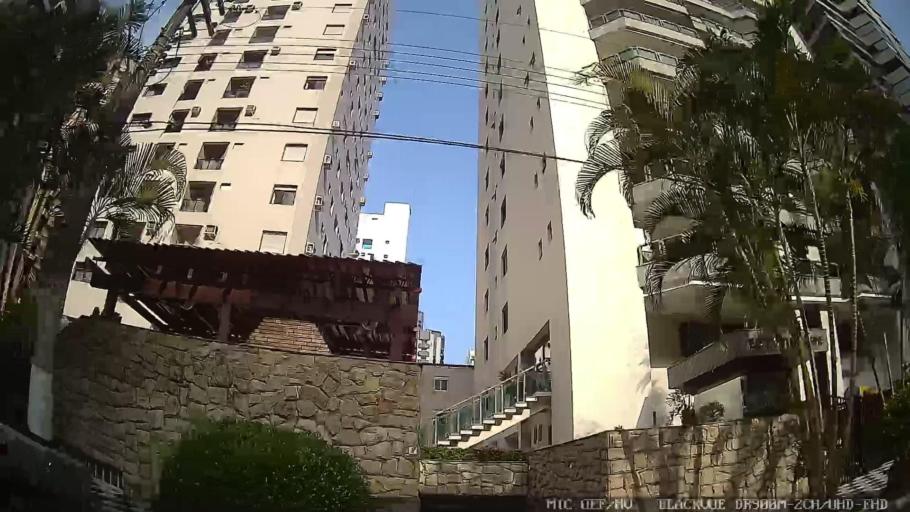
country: BR
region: Sao Paulo
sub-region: Guaruja
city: Guaruja
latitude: -23.9964
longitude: -46.2643
